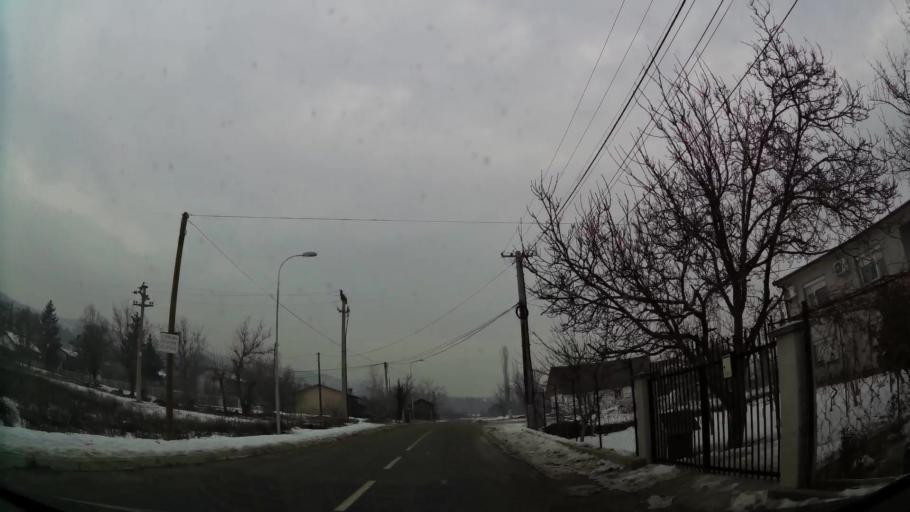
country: MK
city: Kondovo
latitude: 42.0507
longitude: 21.3470
